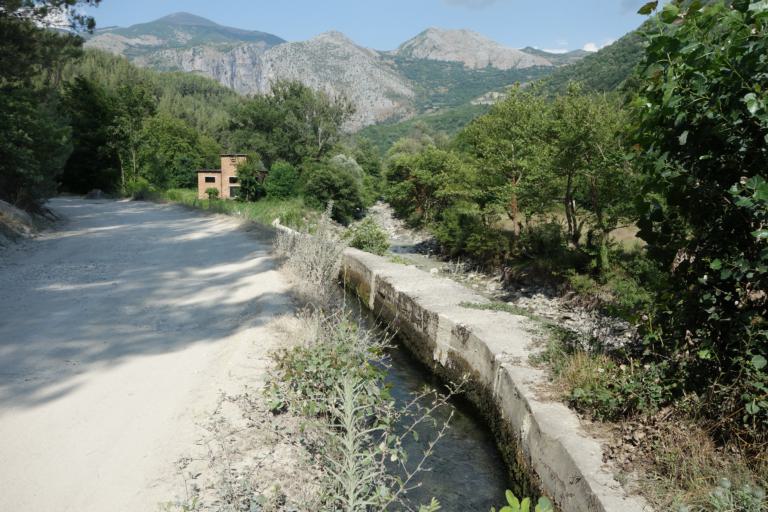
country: AL
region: Berat
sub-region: Rrethi i Skraparit
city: Corovode
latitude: 40.5139
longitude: 20.2339
